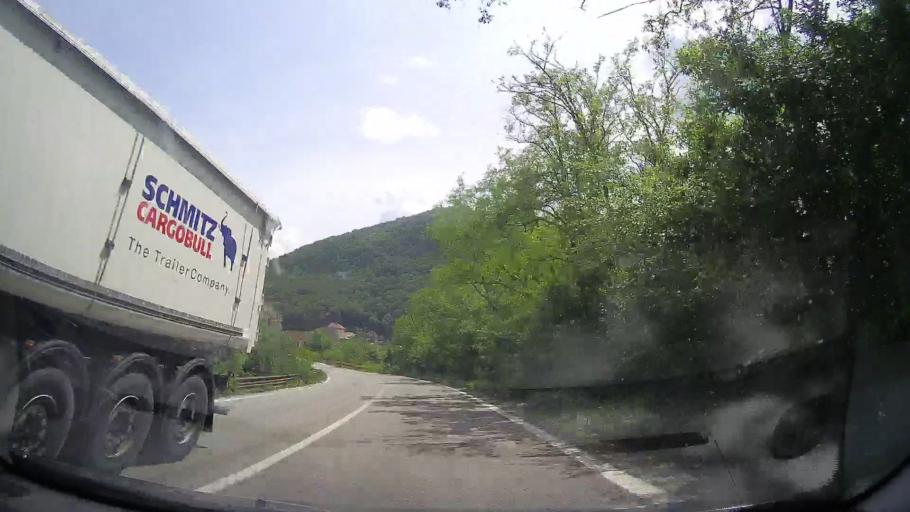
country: RO
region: Valcea
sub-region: Oras Calimanesti
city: Calimanesti
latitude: 45.2638
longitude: 24.3235
